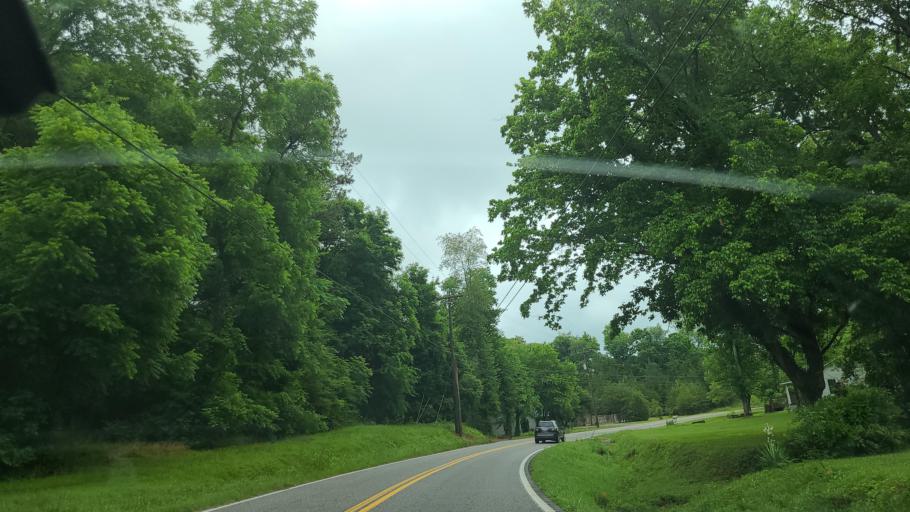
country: US
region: Tennessee
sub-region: Rhea County
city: Dayton
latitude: 35.5000
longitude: -84.9899
